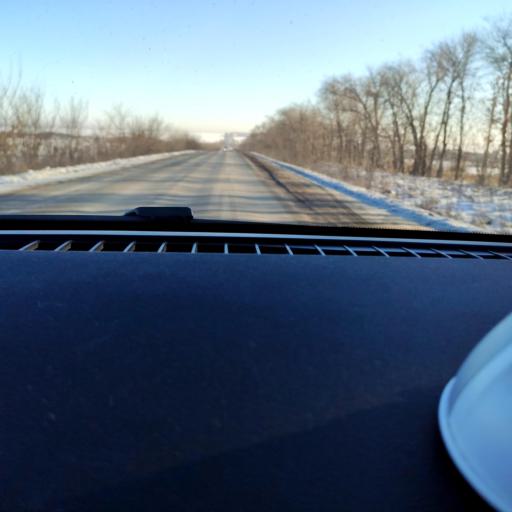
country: RU
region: Samara
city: Spiridonovka
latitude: 53.1446
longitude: 50.5323
